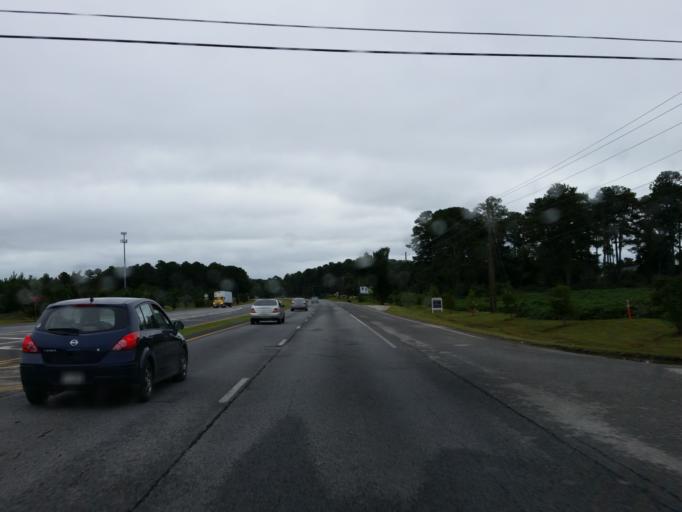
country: US
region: Georgia
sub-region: Clayton County
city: Lovejoy
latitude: 33.4323
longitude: -84.3206
